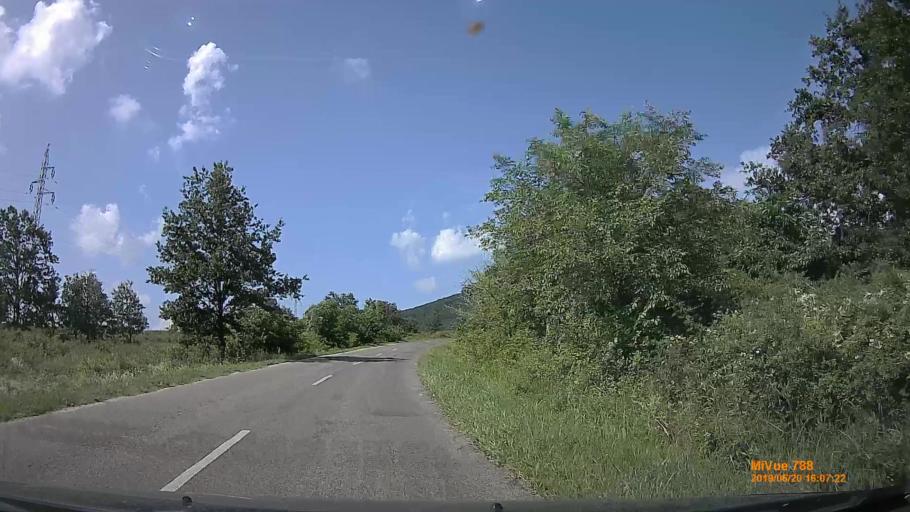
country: HU
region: Baranya
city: Pellerd
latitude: 46.0865
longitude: 18.1111
